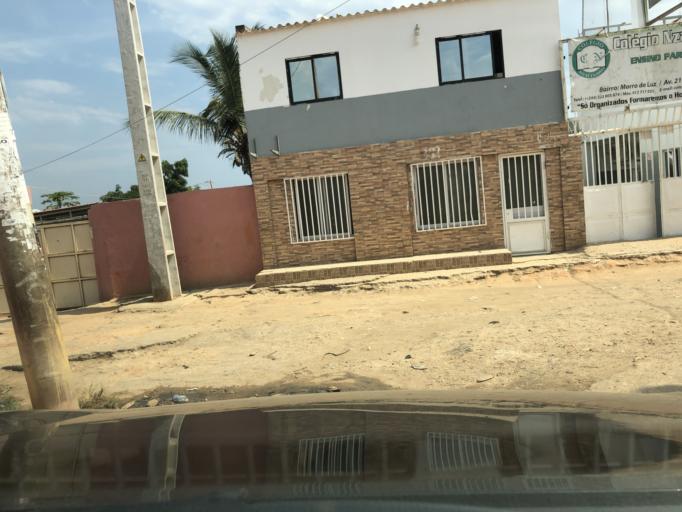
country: AO
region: Luanda
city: Luanda
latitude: -8.8735
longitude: 13.2095
